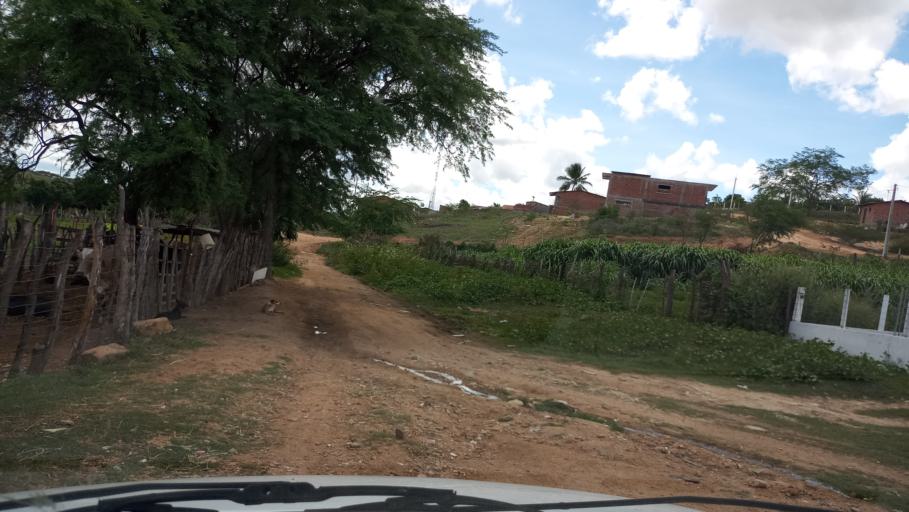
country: BR
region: Rio Grande do Norte
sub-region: Sao Paulo Do Potengi
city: Sao Paulo do Potengi
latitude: -5.8958
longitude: -35.7708
